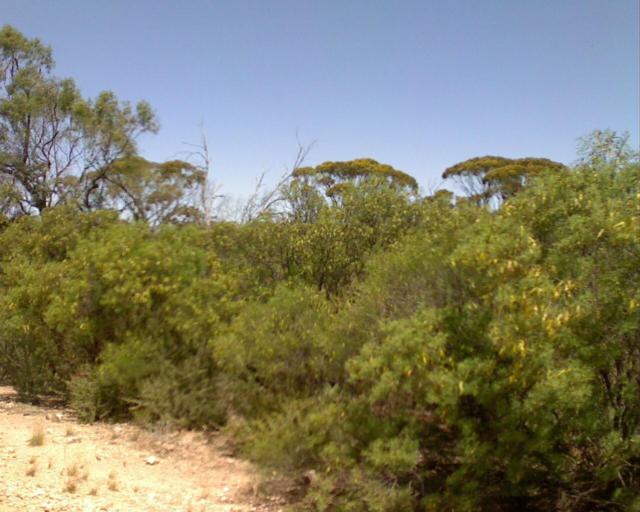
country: AU
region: South Australia
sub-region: Kimba
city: Caralue
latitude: -32.9439
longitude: 135.2762
